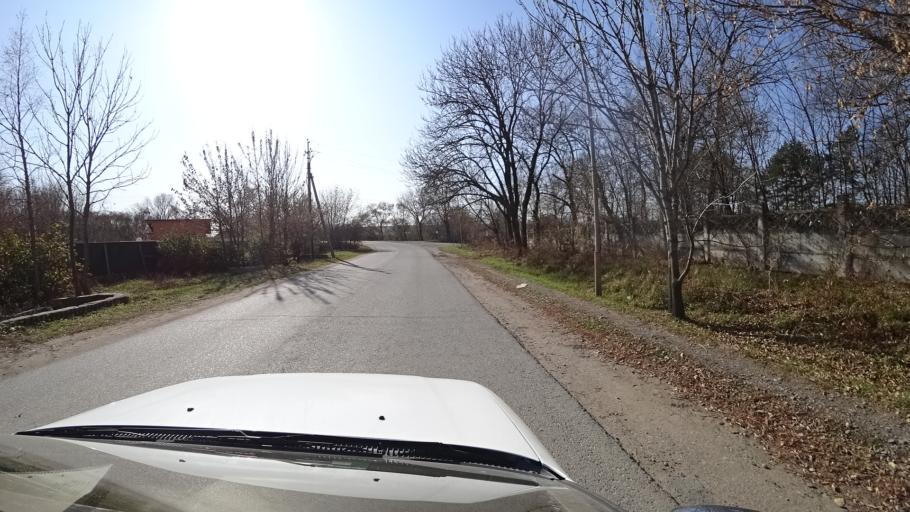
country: RU
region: Primorskiy
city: Dal'nerechensk
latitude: 45.9305
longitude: 133.7236
